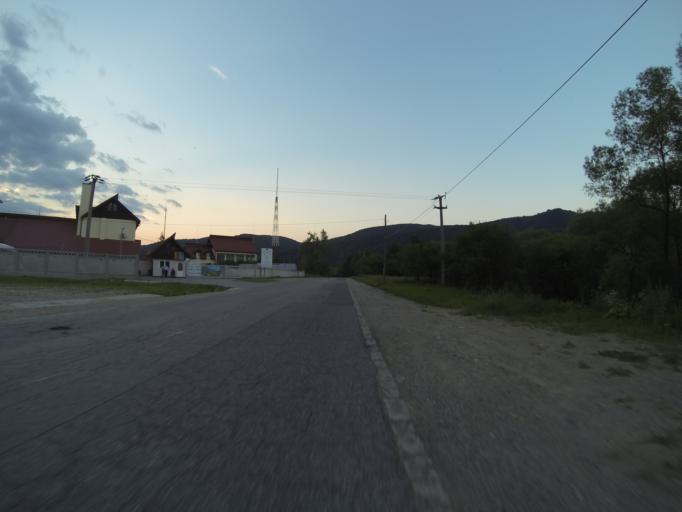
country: RO
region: Brasov
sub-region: Comuna Sinca Noua
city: Sinca Noua
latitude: 45.7281
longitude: 25.2353
